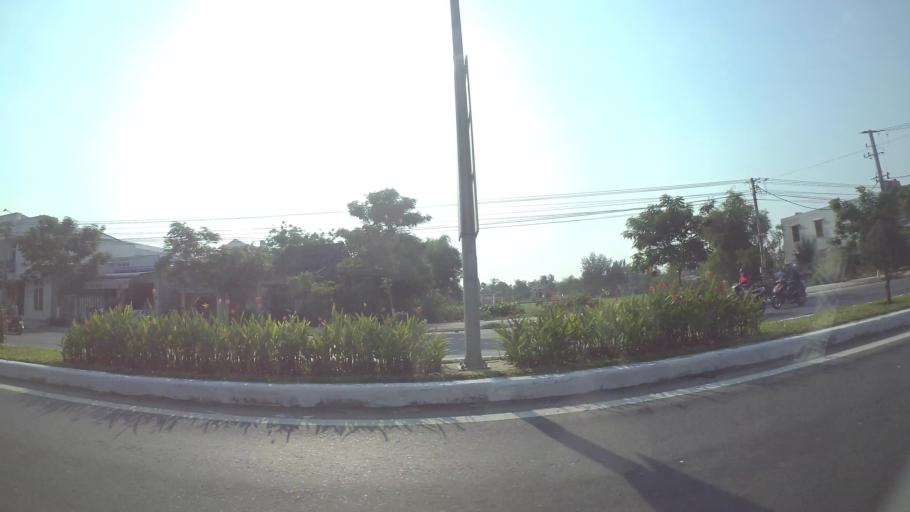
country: VN
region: Quang Nam
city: Quang Nam
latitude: 15.9491
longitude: 108.2547
